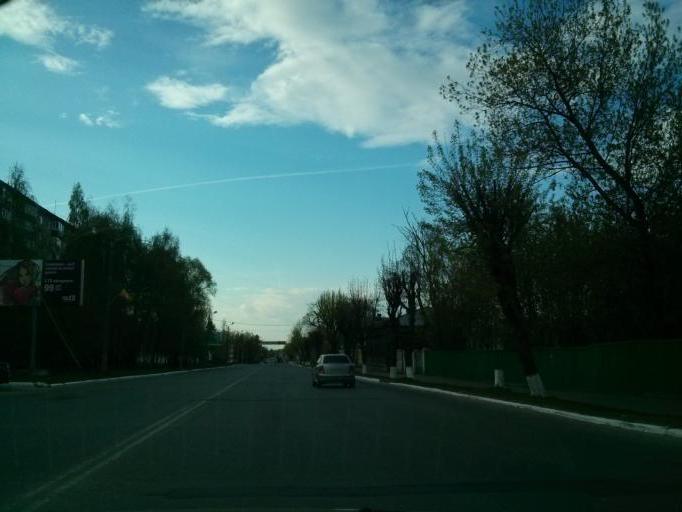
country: RU
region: Vladimir
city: Murom
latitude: 55.5734
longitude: 42.0566
